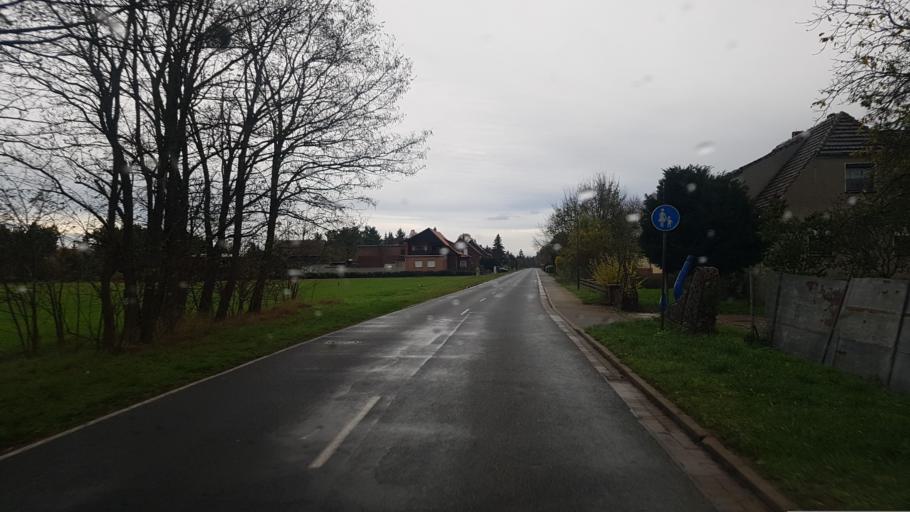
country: DE
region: Saxony-Anhalt
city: Muhlanger
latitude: 51.8621
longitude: 12.7496
